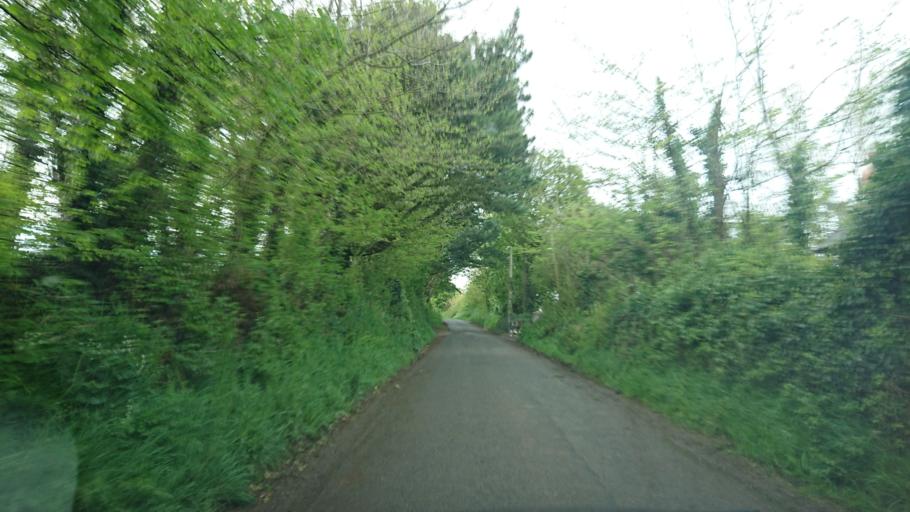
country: IE
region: Munster
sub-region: Waterford
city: Waterford
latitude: 52.2291
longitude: -7.1294
